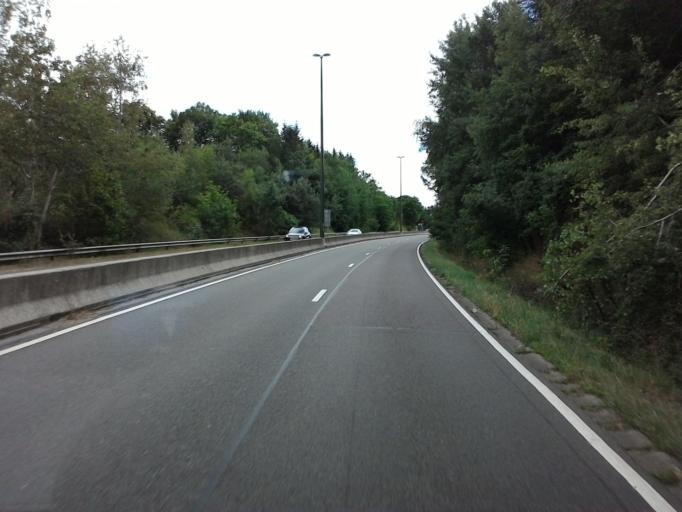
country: BE
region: Wallonia
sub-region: Province du Luxembourg
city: Attert
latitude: 49.7176
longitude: 5.8012
